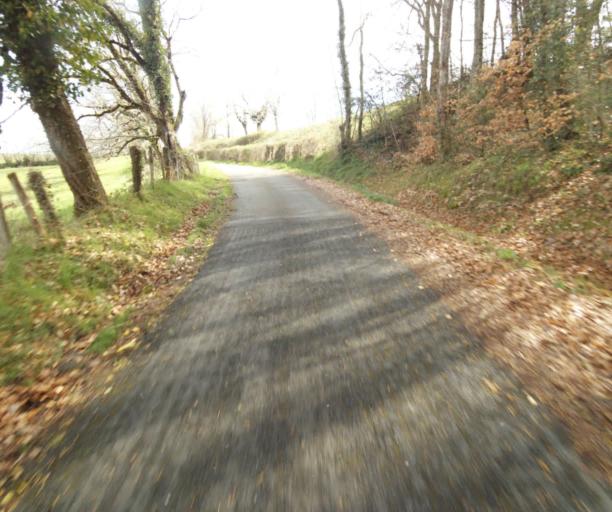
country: FR
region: Limousin
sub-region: Departement de la Correze
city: Laguenne
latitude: 45.2622
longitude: 1.8046
